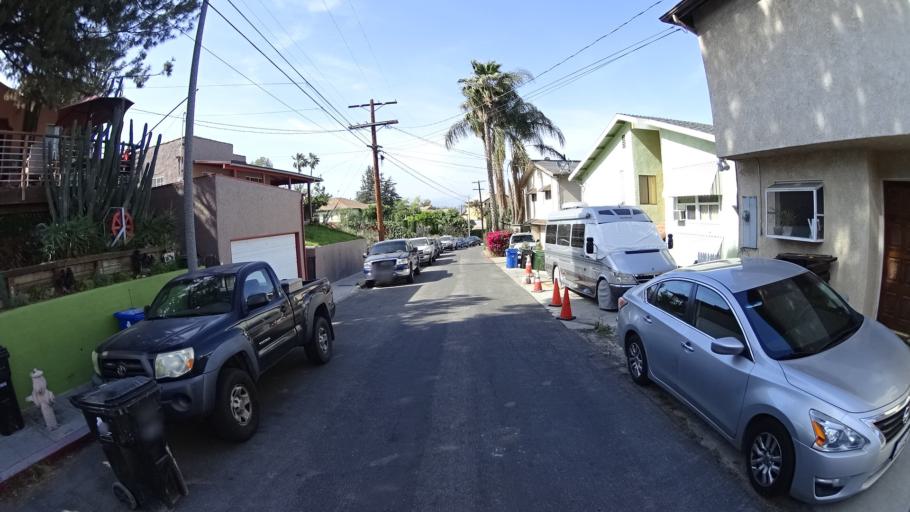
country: US
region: California
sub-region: Los Angeles County
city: Belvedere
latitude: 34.0731
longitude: -118.1771
